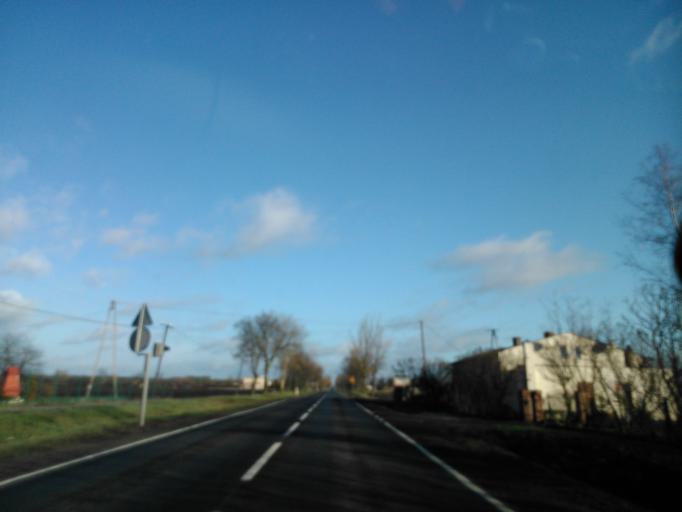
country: PL
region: Kujawsko-Pomorskie
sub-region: Powiat inowroclawski
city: Wierzchoslawice
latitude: 52.8686
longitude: 18.3667
